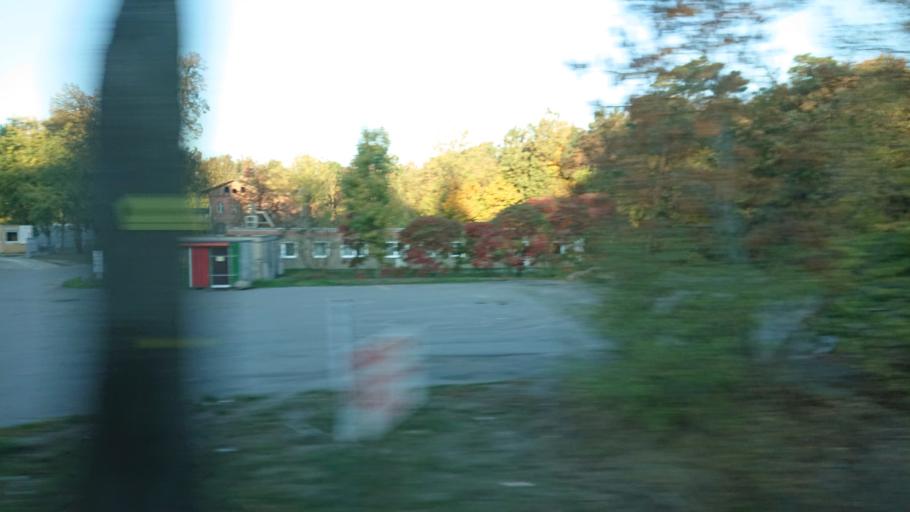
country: DE
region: Mecklenburg-Vorpommern
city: Trollenhagen
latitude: 53.6335
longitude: 13.2655
